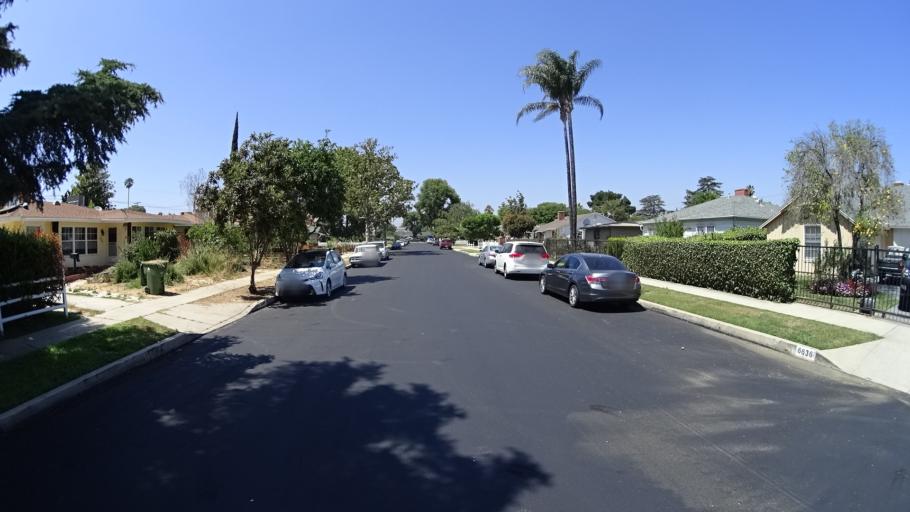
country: US
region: California
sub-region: Los Angeles County
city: Van Nuys
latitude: 34.1914
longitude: -118.4389
